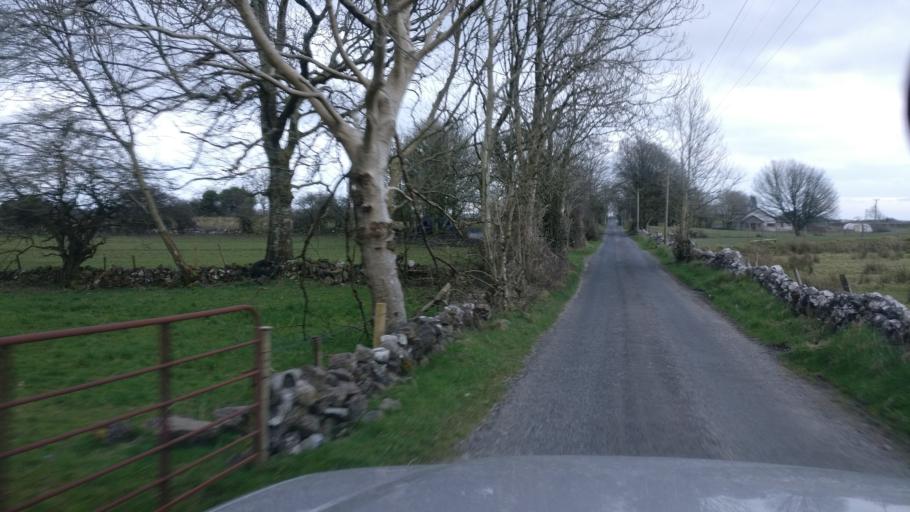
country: IE
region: Connaught
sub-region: County Galway
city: Loughrea
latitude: 53.2595
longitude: -8.4500
